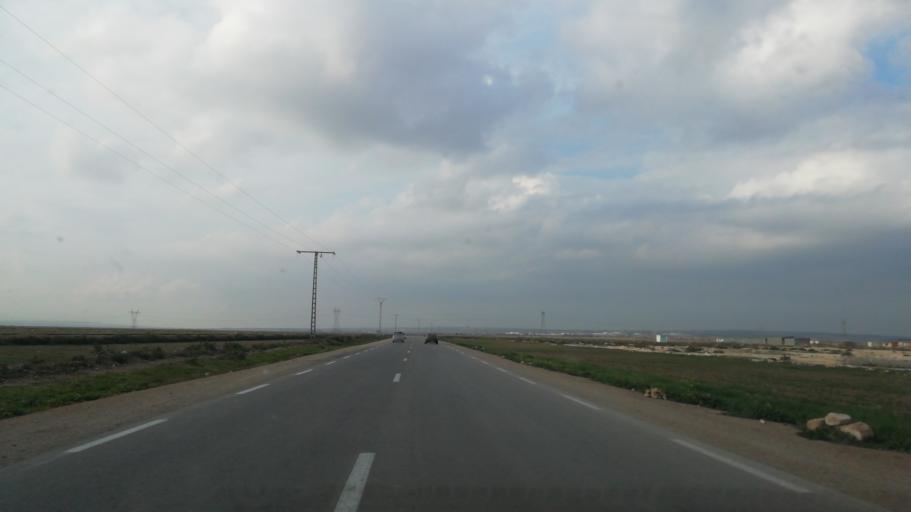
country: DZ
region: Mascara
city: Sig
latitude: 35.6966
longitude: -0.0223
